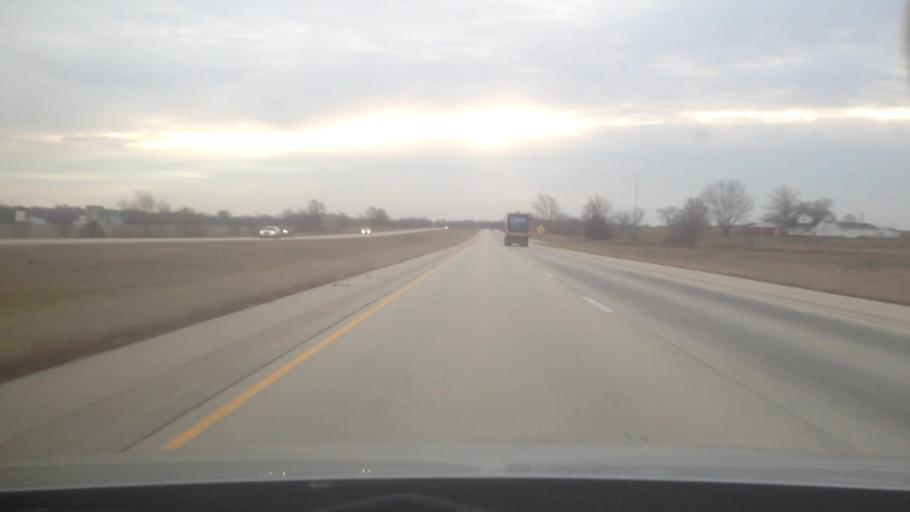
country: US
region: Illinois
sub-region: Macon County
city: Decatur
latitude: 39.7980
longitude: -89.0050
